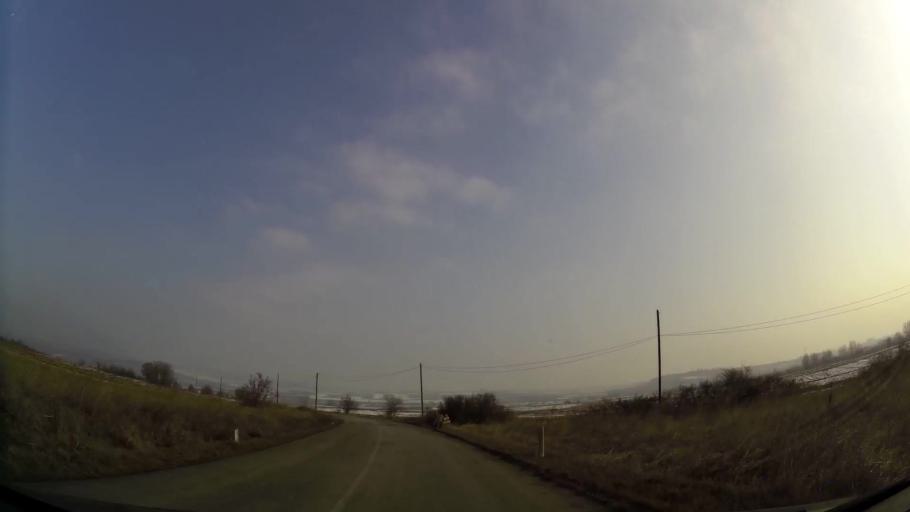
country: MK
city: Miladinovci
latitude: 41.9730
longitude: 21.6334
